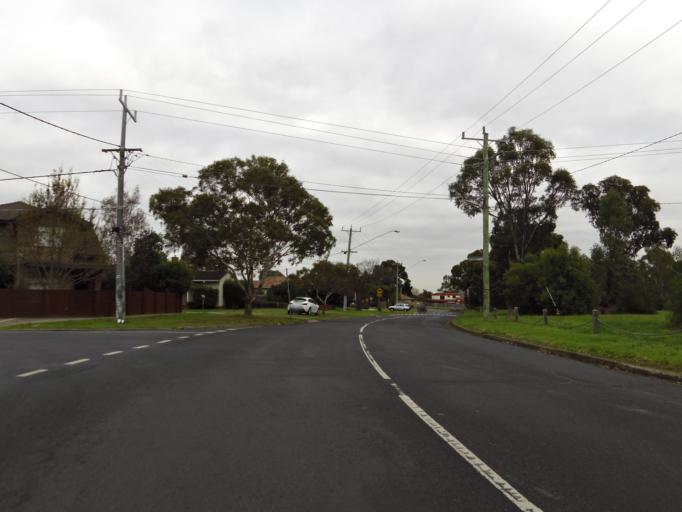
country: AU
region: Victoria
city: Heidelberg West
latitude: -37.7498
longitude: 145.0355
